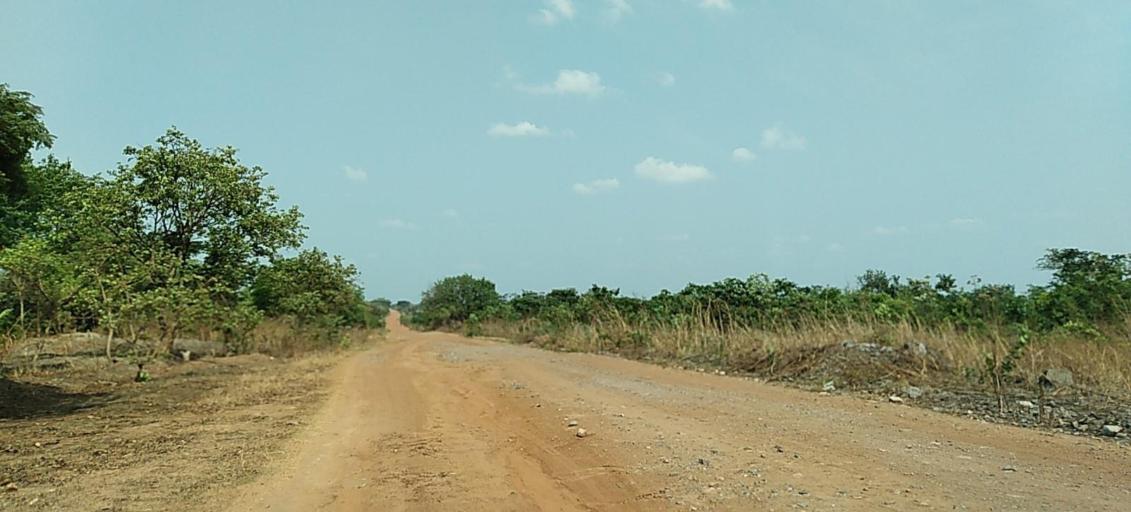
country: ZM
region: Copperbelt
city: Luanshya
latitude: -13.0919
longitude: 28.2988
